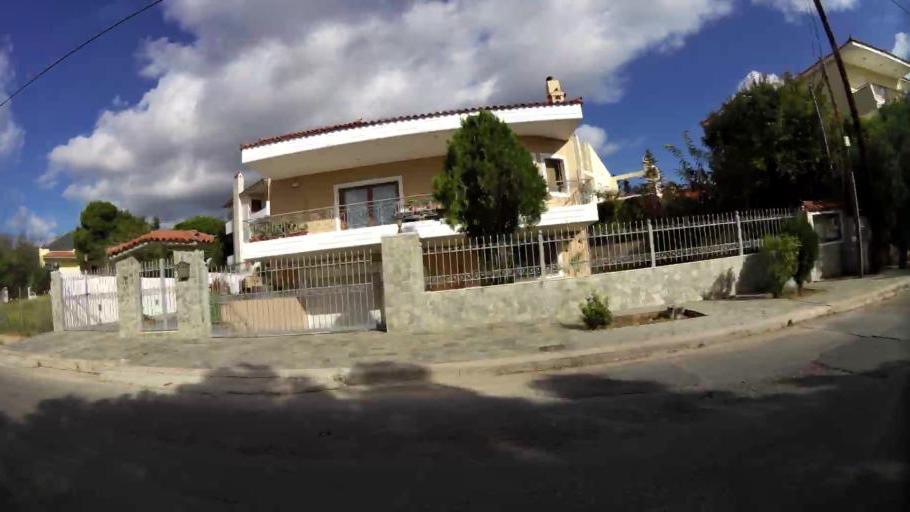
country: GR
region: Attica
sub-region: Nomarchia Anatolikis Attikis
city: Thrakomakedones
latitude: 38.1203
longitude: 23.7585
